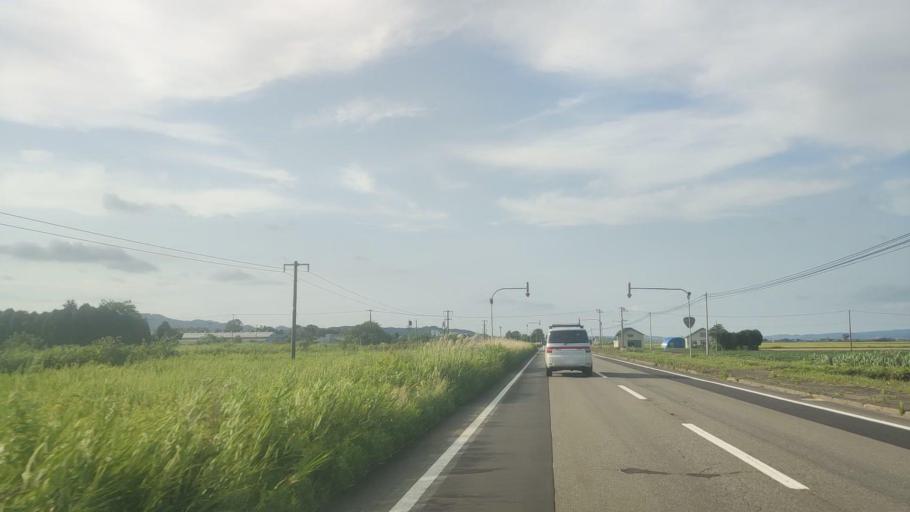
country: JP
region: Hokkaido
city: Chitose
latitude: 42.9609
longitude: 141.7977
